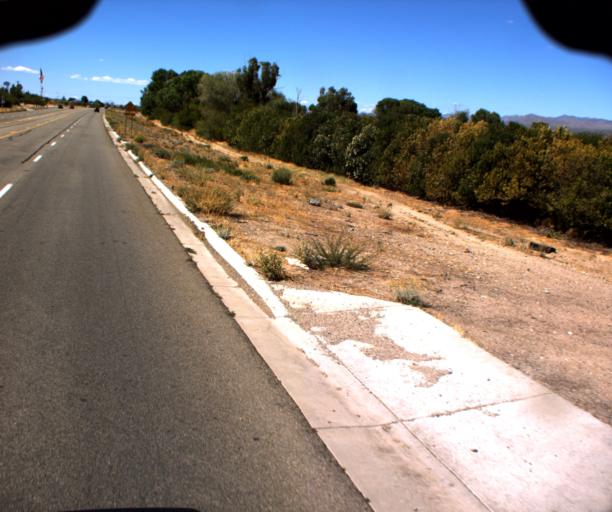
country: US
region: Arizona
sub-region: Yavapai County
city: Bagdad
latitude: 34.7092
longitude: -113.6130
